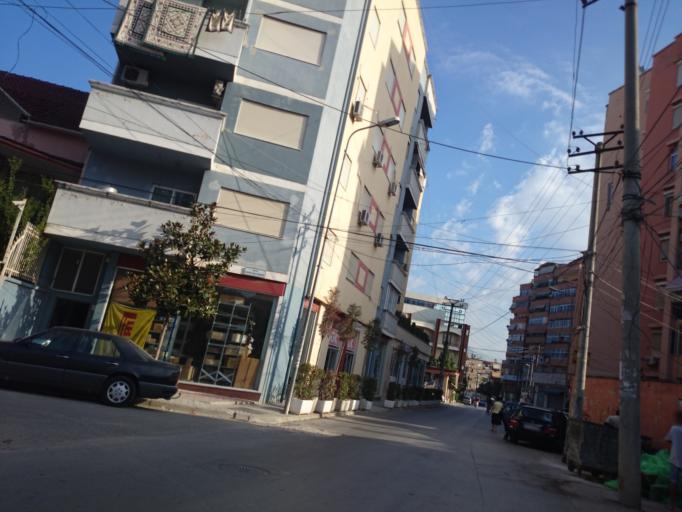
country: AL
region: Tirane
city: Tirana
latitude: 41.3179
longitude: 19.7989
